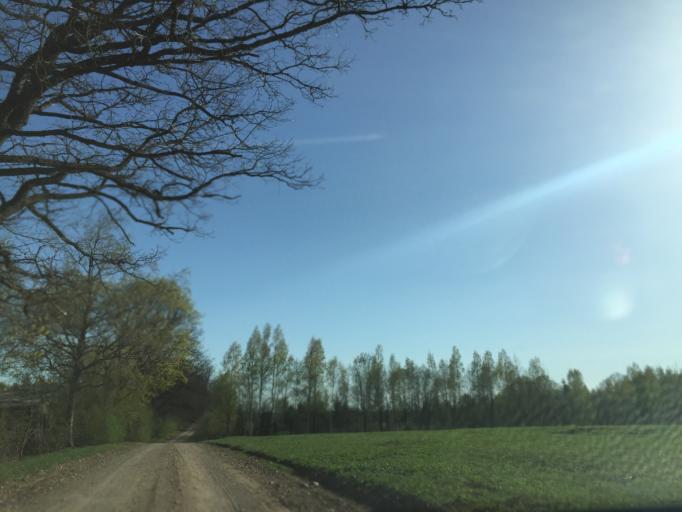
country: LV
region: Ergli
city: Ergli
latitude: 56.8784
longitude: 25.4849
